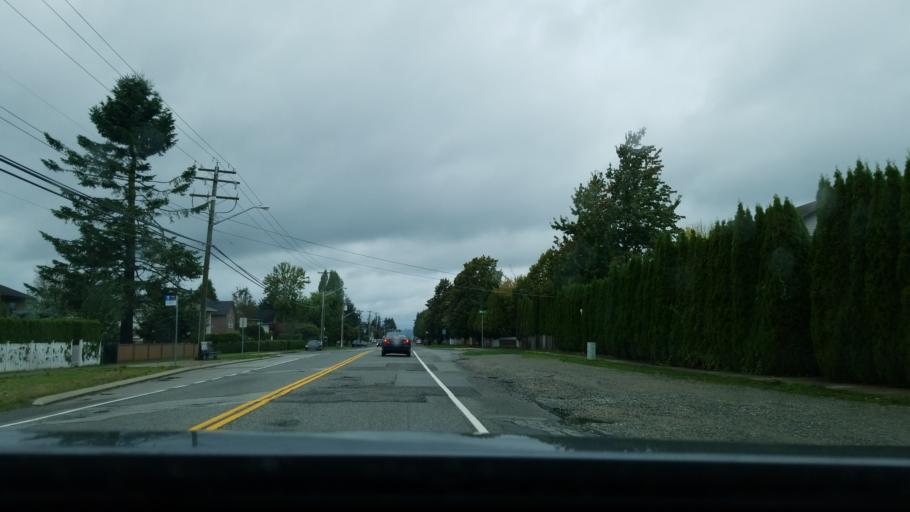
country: CA
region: British Columbia
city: Langley
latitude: 49.1189
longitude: -122.7062
